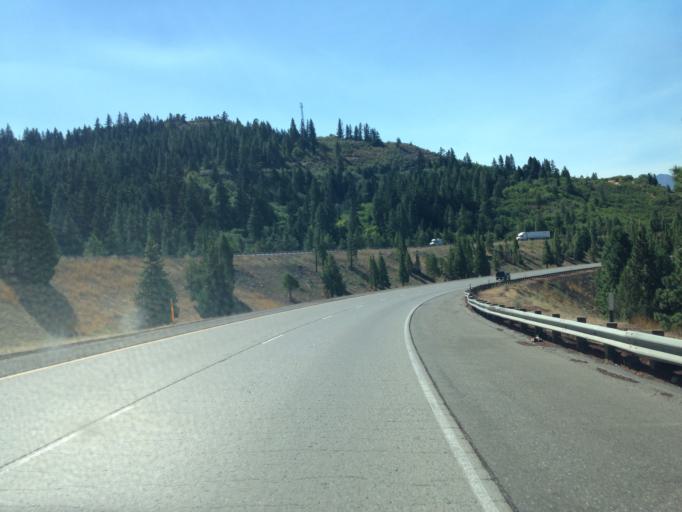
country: US
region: Oregon
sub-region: Jackson County
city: Ashland
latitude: 42.0399
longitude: -122.5990
